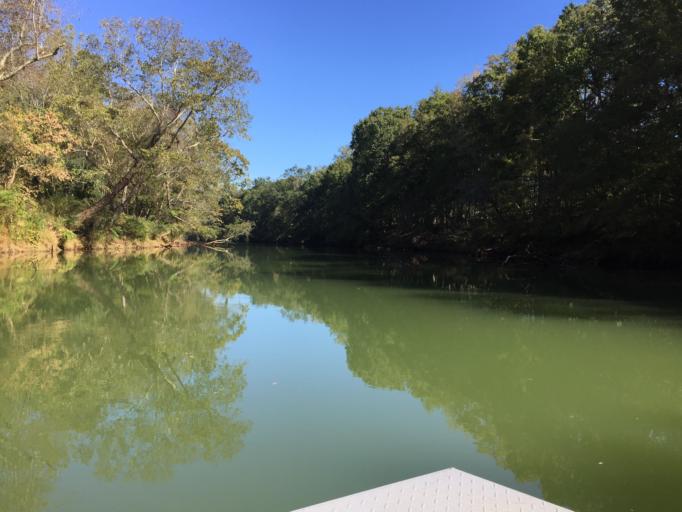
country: US
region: Georgia
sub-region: Gwinnett County
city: Berkeley Lake
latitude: 33.9989
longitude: -84.1807
